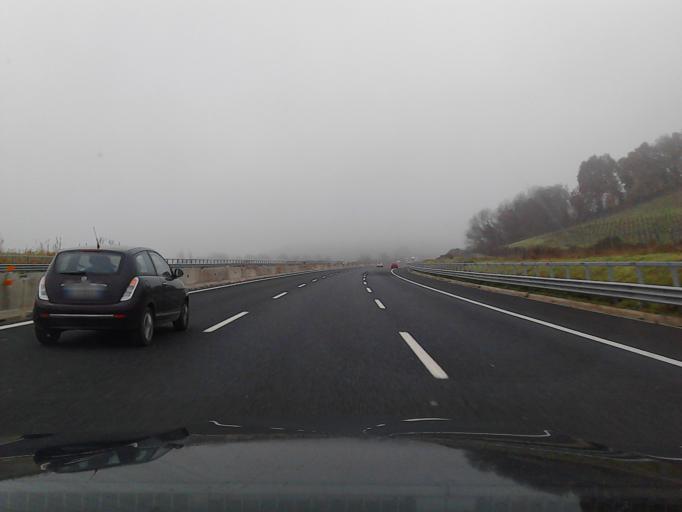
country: IT
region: The Marches
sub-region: Provincia di Pesaro e Urbino
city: Gradara
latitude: 43.9478
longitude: 12.7738
